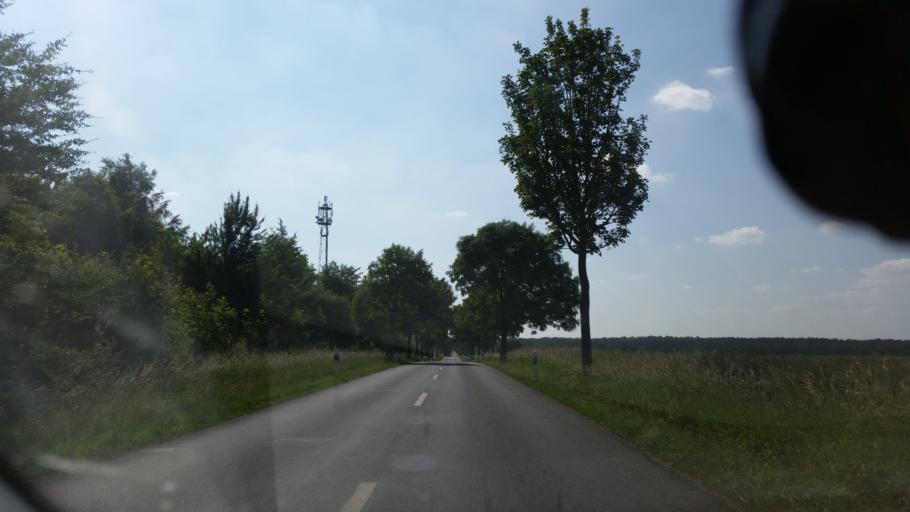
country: DE
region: Lower Saxony
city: Lehre
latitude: 52.3142
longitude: 10.7467
